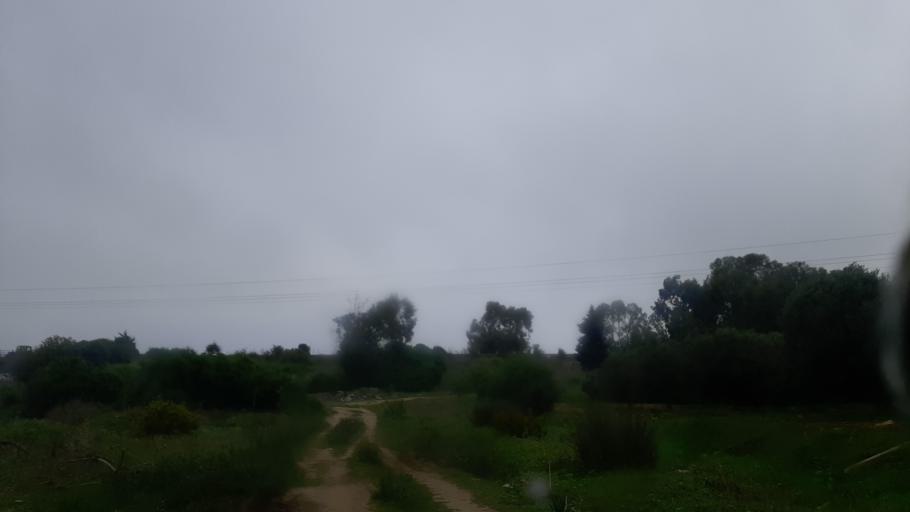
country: TN
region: Nabul
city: Qulaybiyah
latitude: 36.8229
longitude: 11.0468
